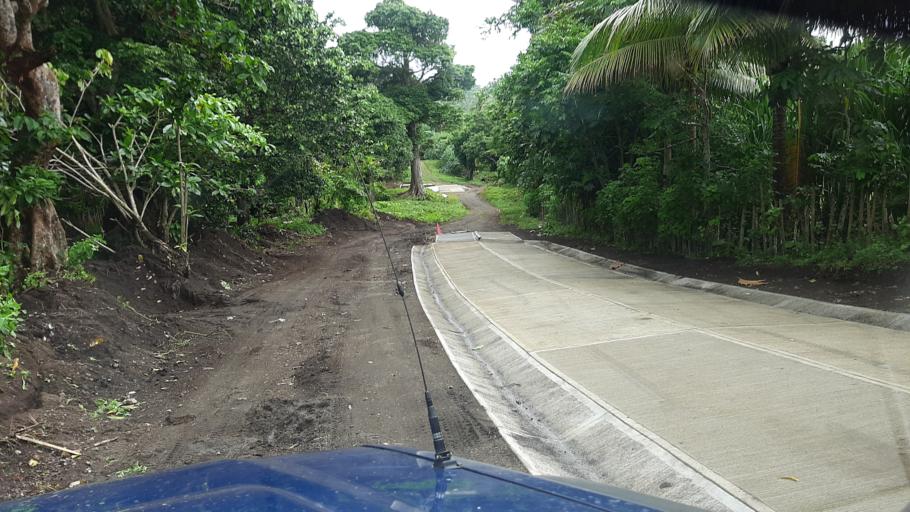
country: VU
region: Shefa
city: Port-Vila
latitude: -16.9006
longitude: 168.5685
